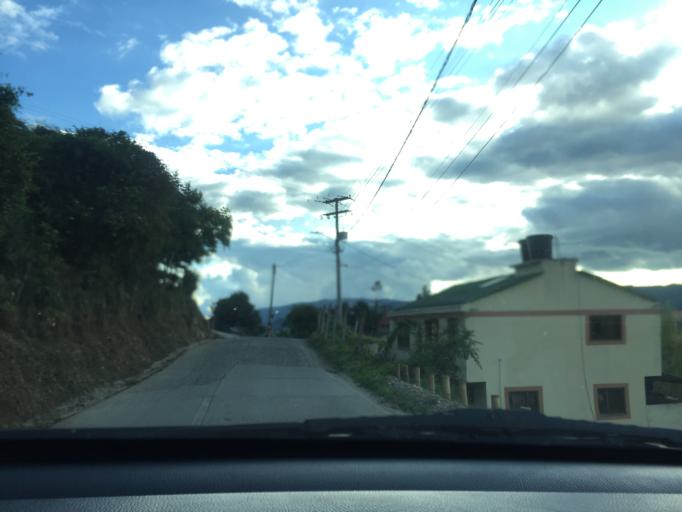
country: CO
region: Cundinamarca
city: Sopo
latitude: 4.9135
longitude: -73.9352
